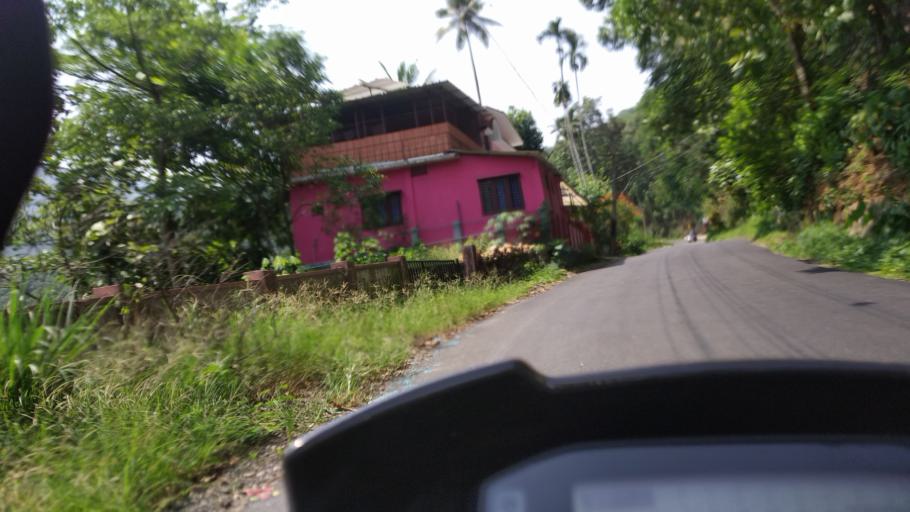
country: IN
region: Kerala
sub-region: Kottayam
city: Erattupetta
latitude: 9.6905
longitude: 76.8528
